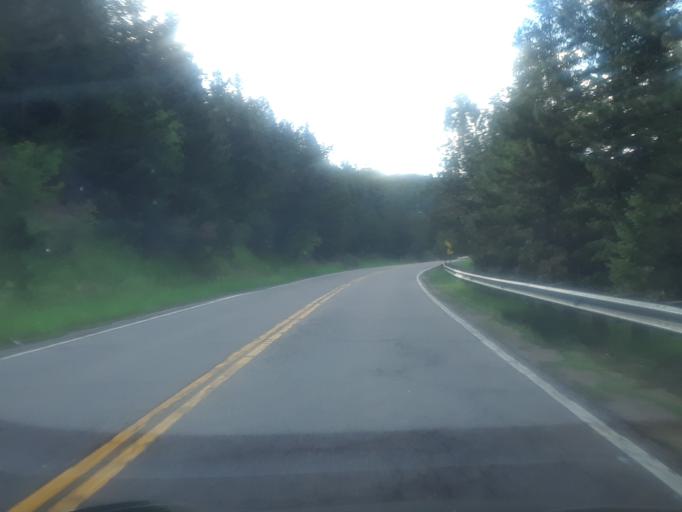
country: US
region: Colorado
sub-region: Jefferson County
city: Kittredge
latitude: 39.7172
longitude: -105.3540
